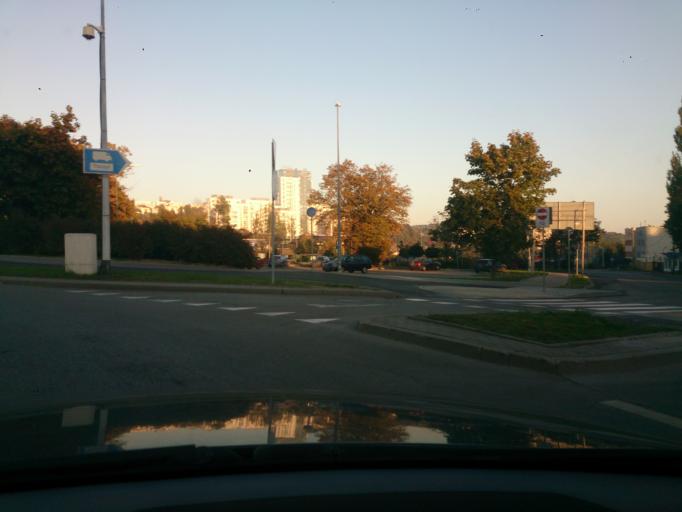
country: PL
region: Pomeranian Voivodeship
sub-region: Gdynia
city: Gdynia
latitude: 54.4913
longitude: 18.5351
